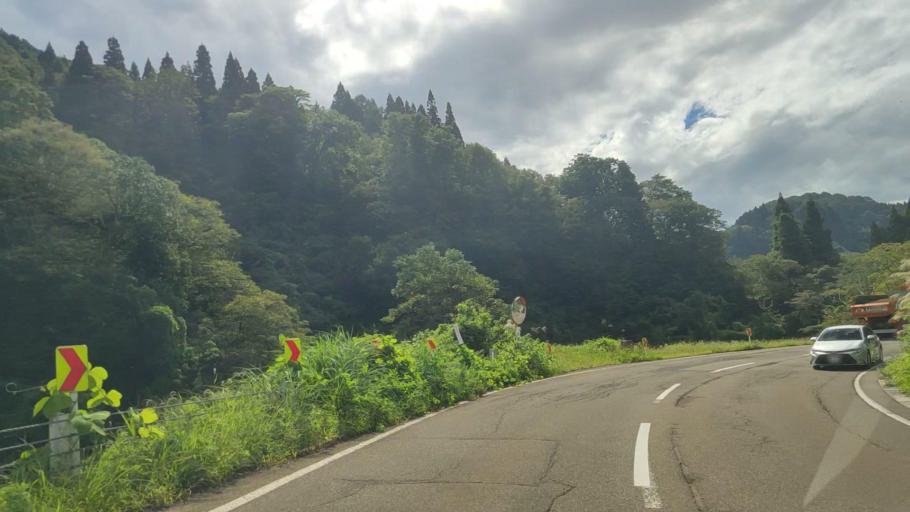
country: JP
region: Niigata
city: Arai
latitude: 36.9446
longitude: 138.2917
